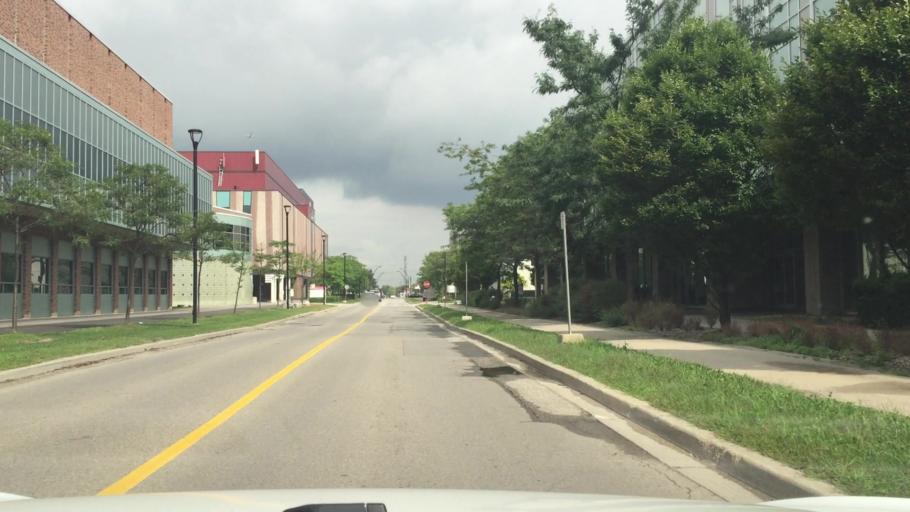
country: CA
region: Ontario
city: Concord
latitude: 43.7715
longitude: -79.4986
